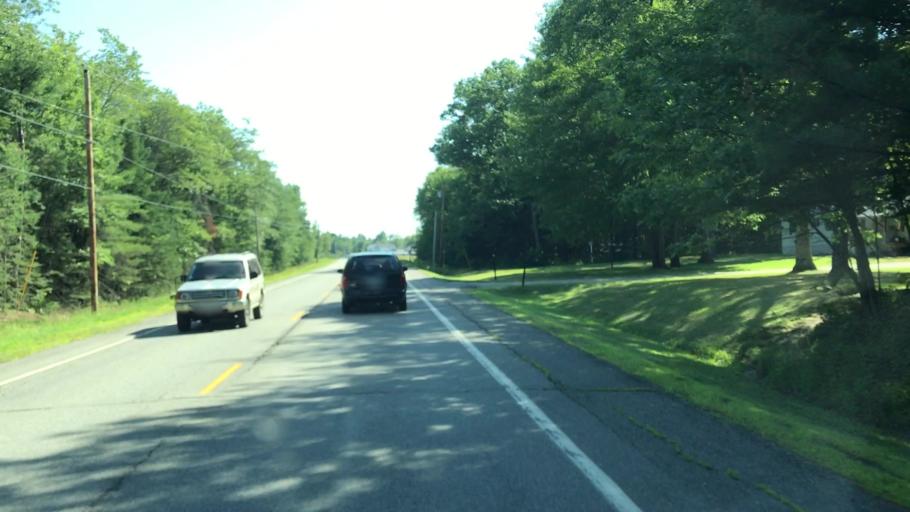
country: US
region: Maine
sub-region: Penobscot County
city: Enfield
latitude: 45.3012
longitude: -68.6165
